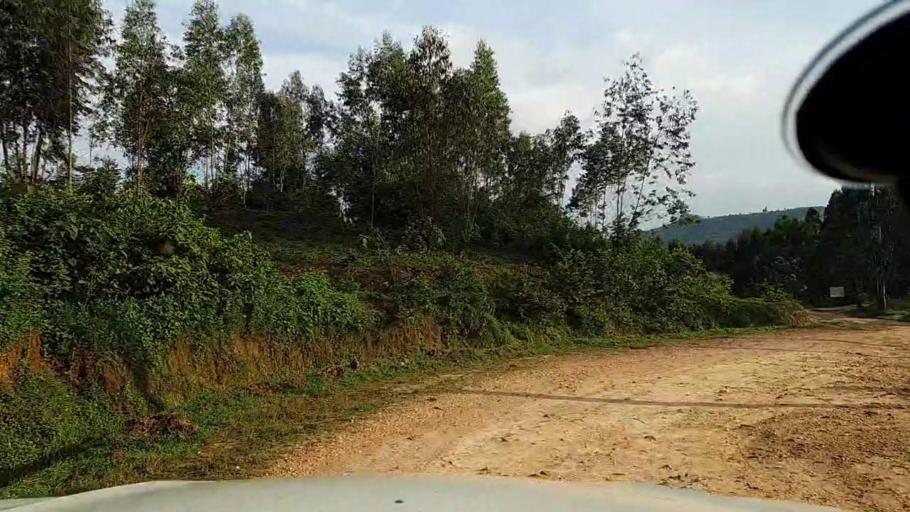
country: RW
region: Southern Province
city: Gitarama
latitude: -2.1897
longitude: 29.5772
